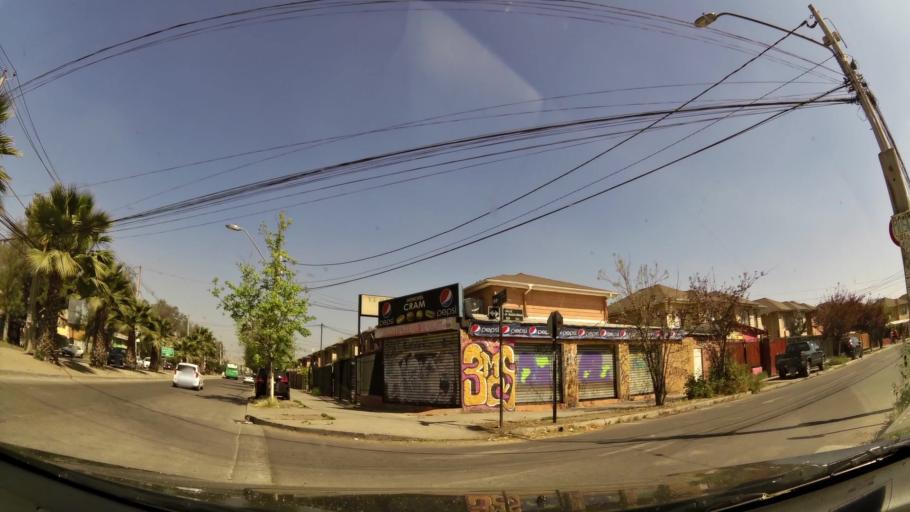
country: CL
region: Santiago Metropolitan
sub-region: Provincia de Santiago
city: Lo Prado
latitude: -33.3587
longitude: -70.7208
